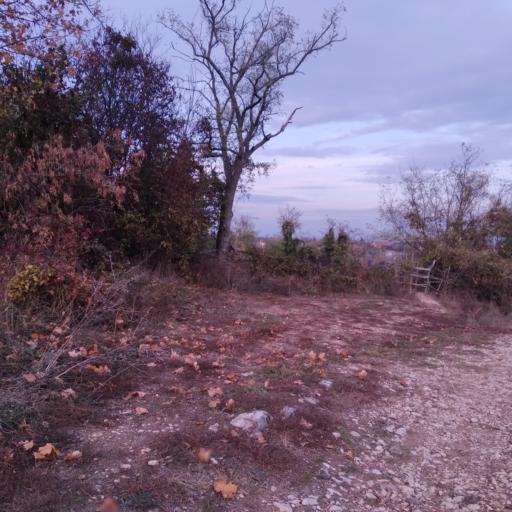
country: HU
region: Pest
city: Pomaz
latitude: 47.6218
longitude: 19.0282
